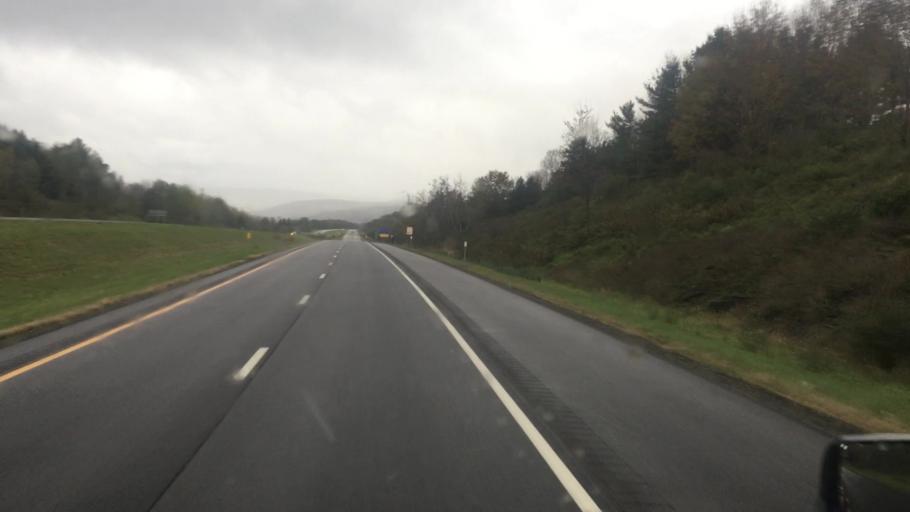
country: US
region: New York
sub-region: Broome County
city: Chenango Bridge
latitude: 42.1868
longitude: -75.7150
